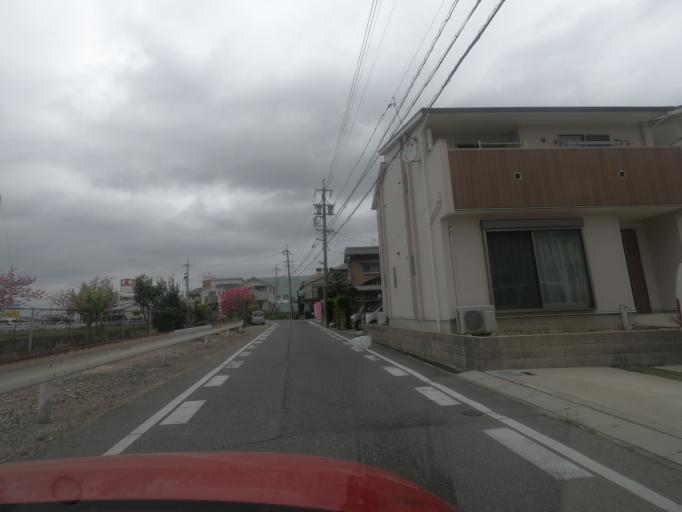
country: JP
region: Aichi
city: Kasugai
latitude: 35.2673
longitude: 136.9545
